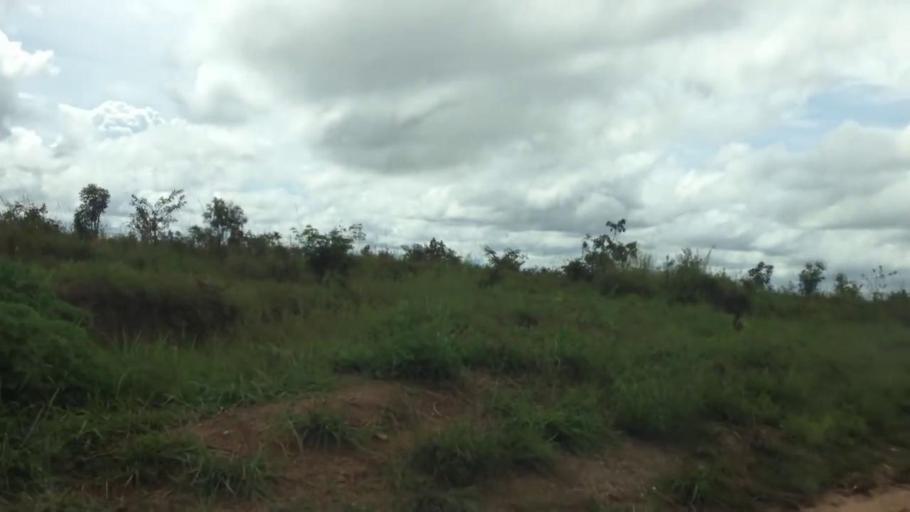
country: CD
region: Katanga
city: Kolwezi
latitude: -10.7488
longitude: 25.5156
